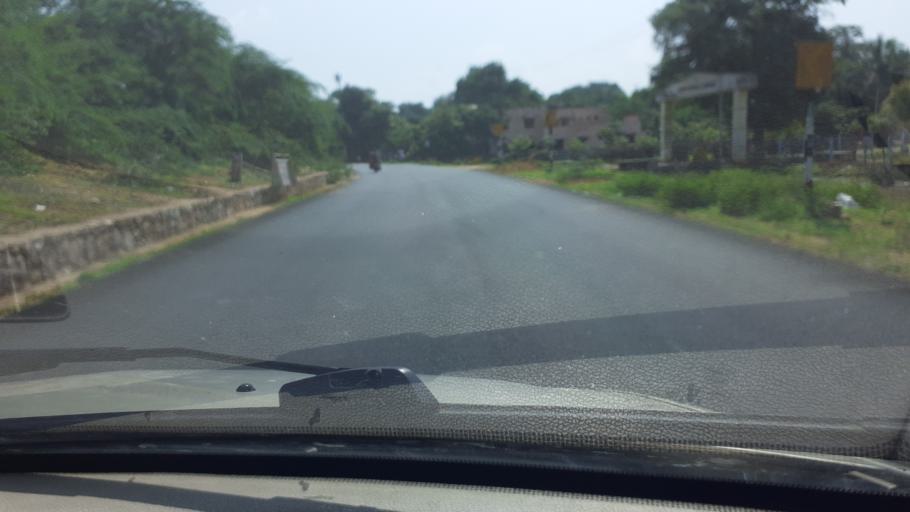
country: IN
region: Tamil Nadu
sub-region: Thoothukkudi
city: Alwar Tirunagari
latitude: 8.6103
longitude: 77.9264
